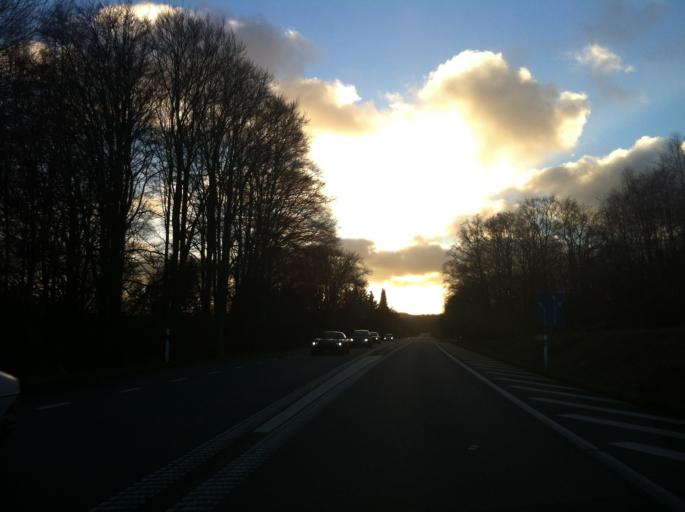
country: SE
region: Skane
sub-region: Hassleholms Kommun
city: Sosdala
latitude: 56.0214
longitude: 13.6731
